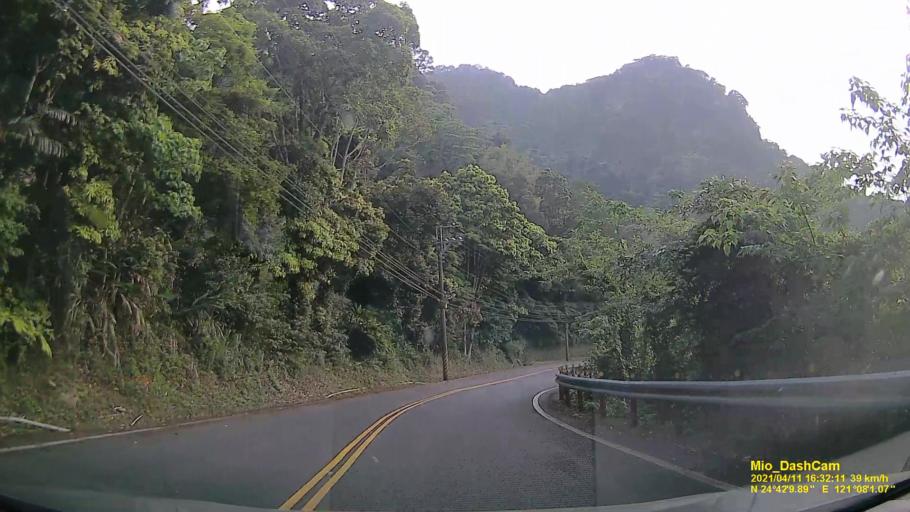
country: TW
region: Taiwan
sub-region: Hsinchu
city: Zhubei
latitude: 24.7027
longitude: 121.1336
